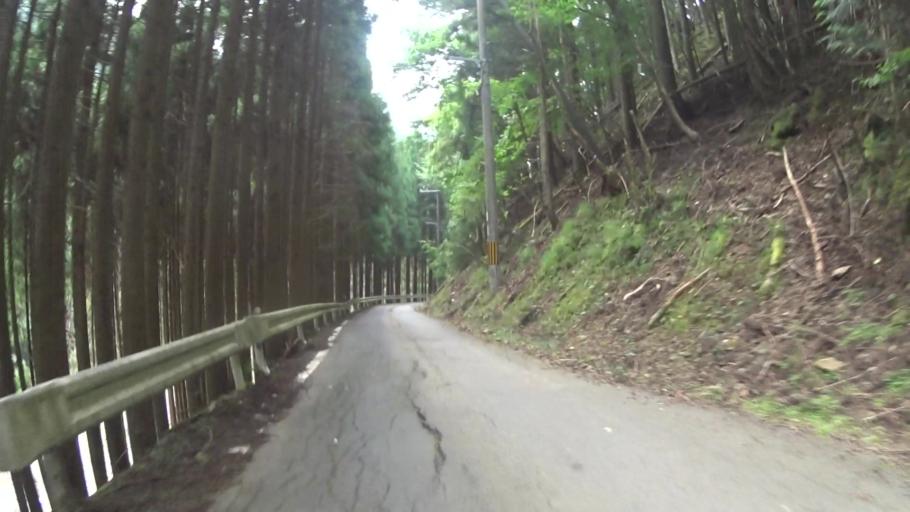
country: JP
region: Kyoto
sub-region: Kyoto-shi
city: Kamigyo-ku
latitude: 35.1801
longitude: 135.7342
